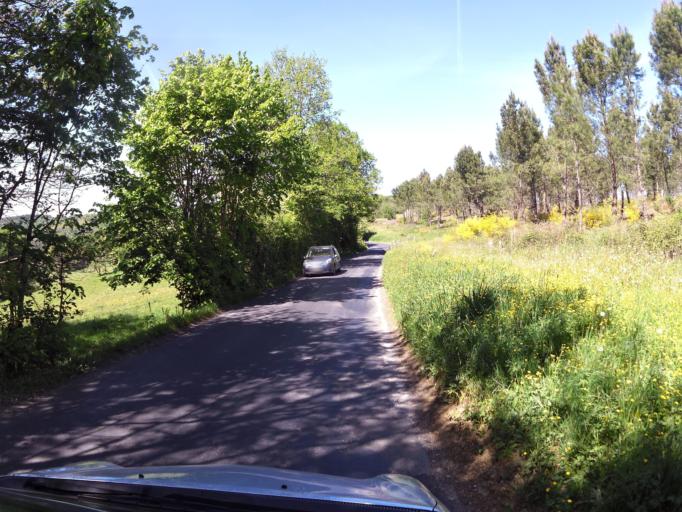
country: FR
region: Aquitaine
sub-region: Departement de la Dordogne
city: Sarlat-la-Caneda
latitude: 44.9123
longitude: 1.1929
